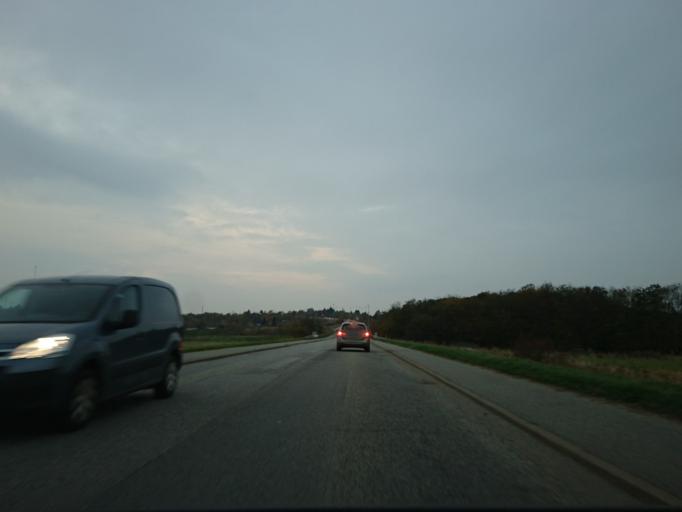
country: DK
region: North Denmark
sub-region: Alborg Kommune
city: Aalborg
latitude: 57.0103
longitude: 9.9105
